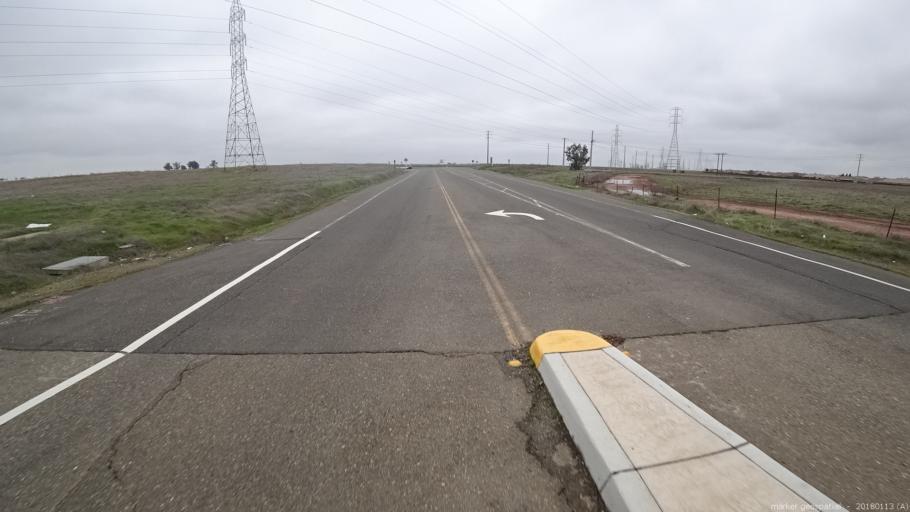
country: US
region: California
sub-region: Sacramento County
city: Gold River
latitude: 38.5606
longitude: -121.2022
